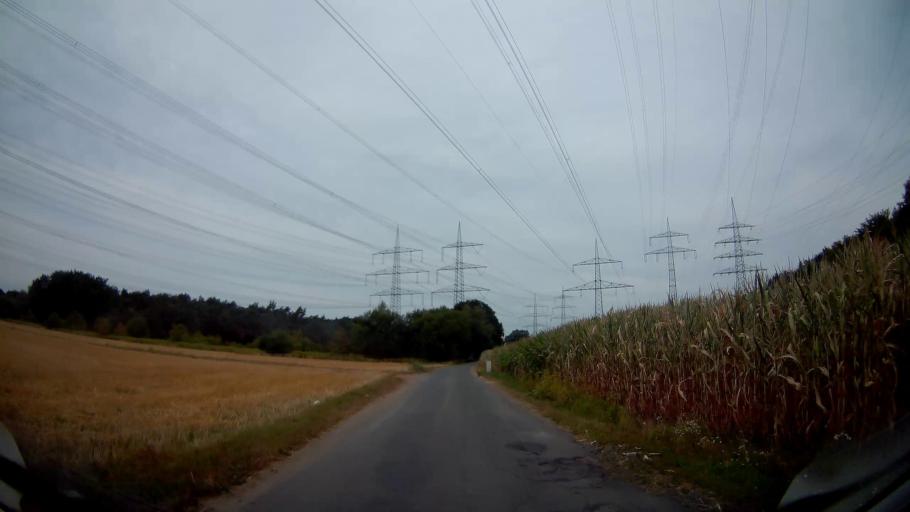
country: DE
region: North Rhine-Westphalia
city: Marl
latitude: 51.6765
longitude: 7.0629
